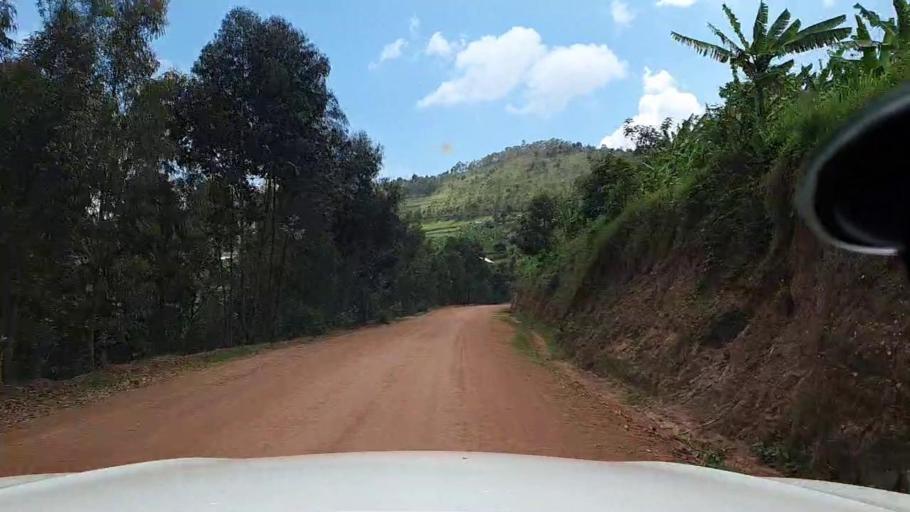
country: RW
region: Kigali
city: Kigali
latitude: -1.7787
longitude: 29.8404
